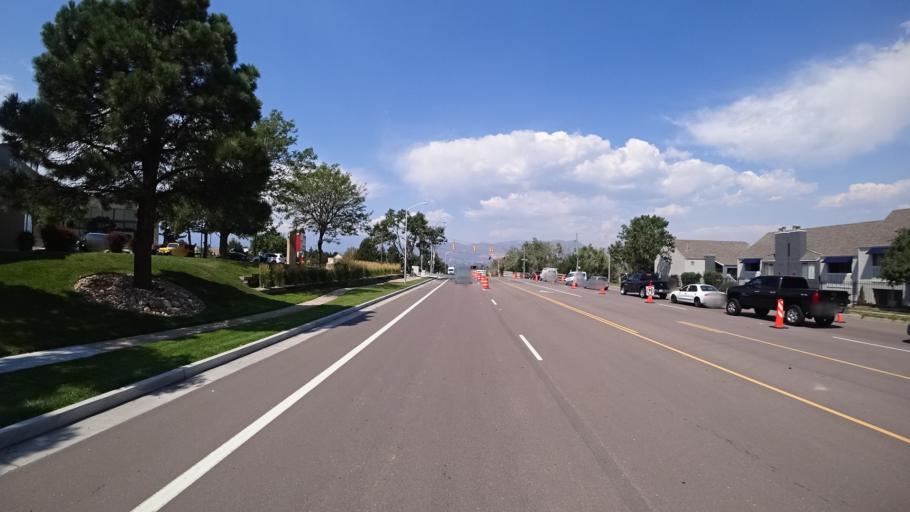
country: US
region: Colorado
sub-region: El Paso County
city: Cimarron Hills
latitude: 38.9258
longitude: -104.7742
